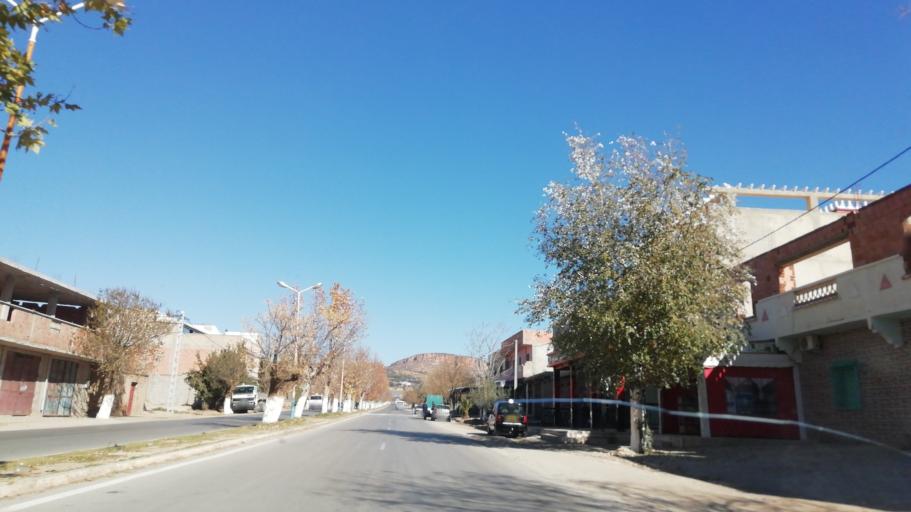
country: DZ
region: Tlemcen
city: Sebdou
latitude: 34.6661
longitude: -1.3207
